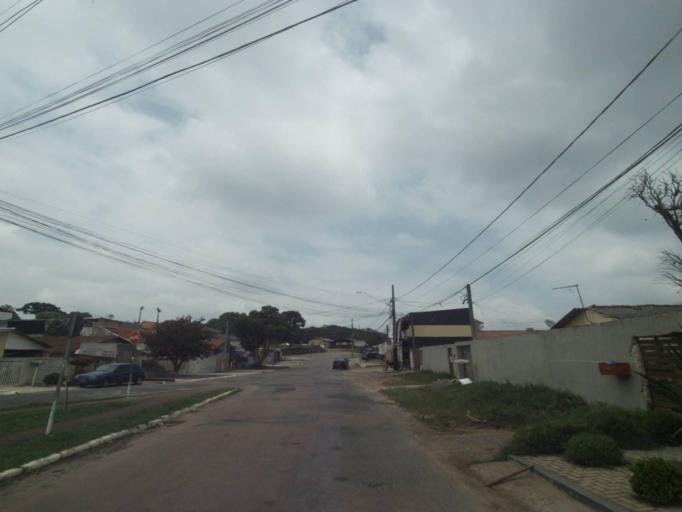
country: BR
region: Parana
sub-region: Curitiba
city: Curitiba
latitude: -25.4849
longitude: -49.3555
